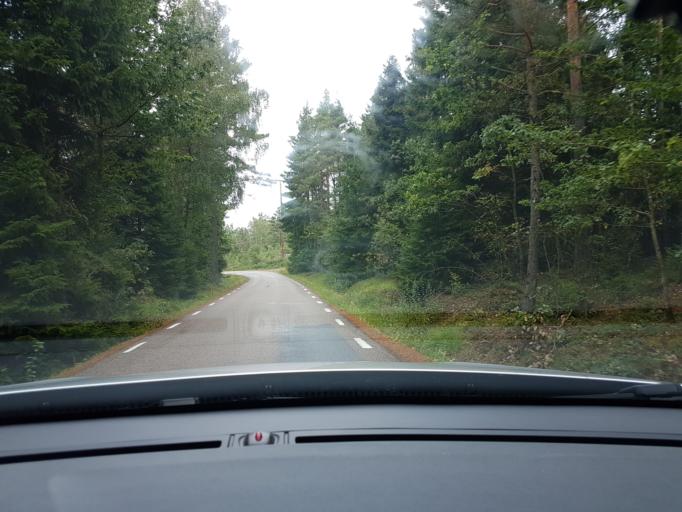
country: SE
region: Vaestra Goetaland
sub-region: Ale Kommun
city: Alvangen
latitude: 57.9061
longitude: 12.1737
